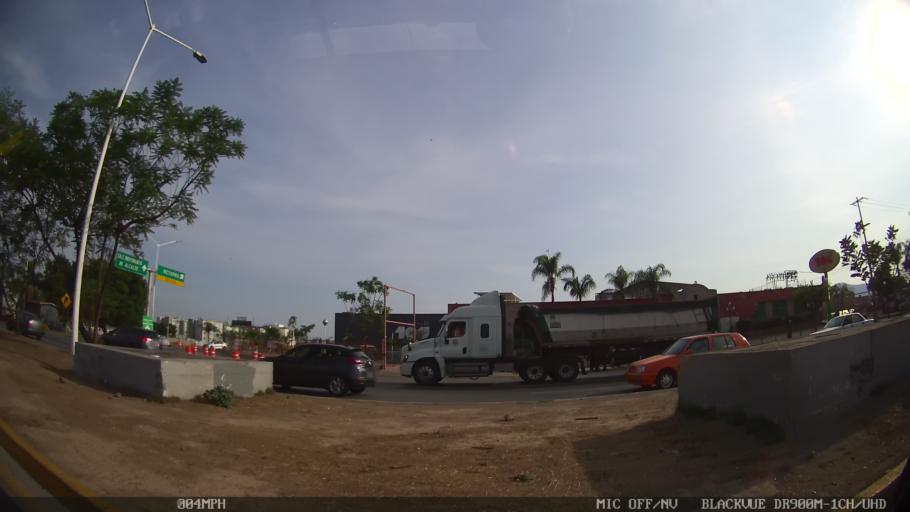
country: MX
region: Jalisco
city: Tlaquepaque
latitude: 20.7126
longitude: -103.2978
